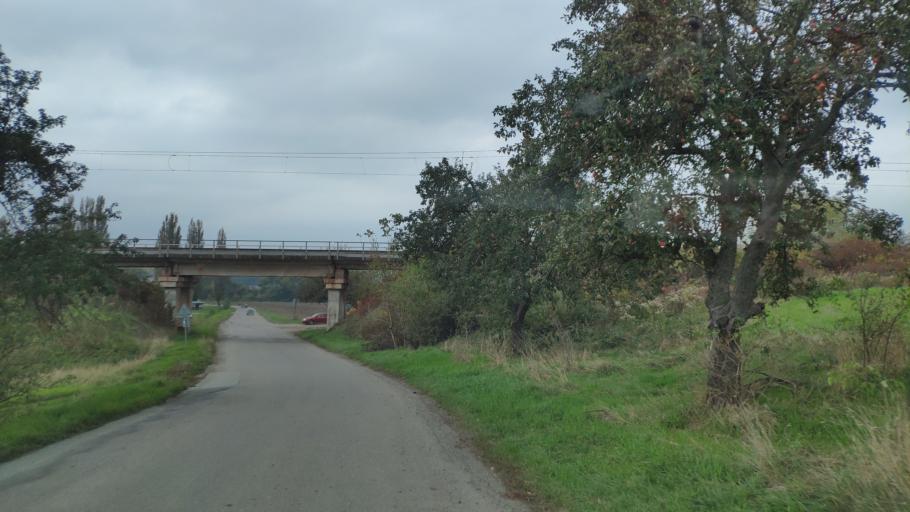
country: SK
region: Kosicky
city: Kosice
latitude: 48.6365
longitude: 21.3804
